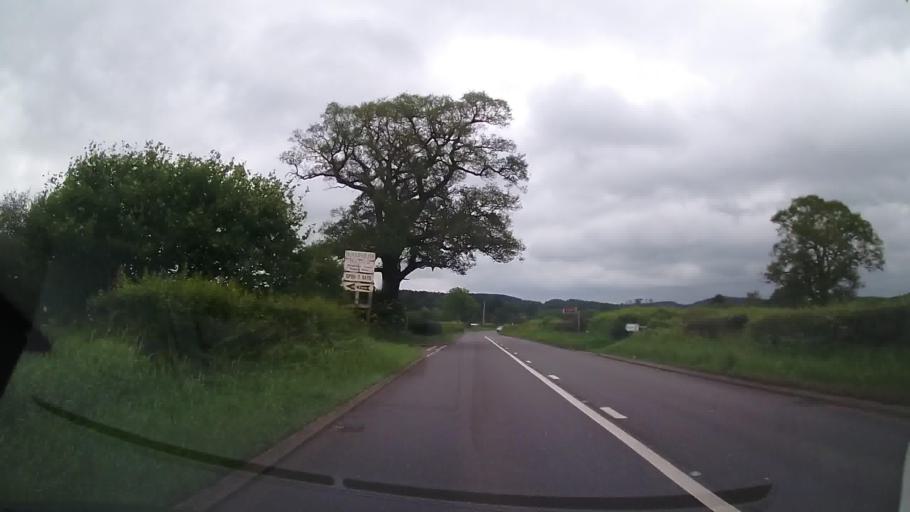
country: GB
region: England
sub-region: Staffordshire
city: Standon
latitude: 52.9418
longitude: -2.3506
